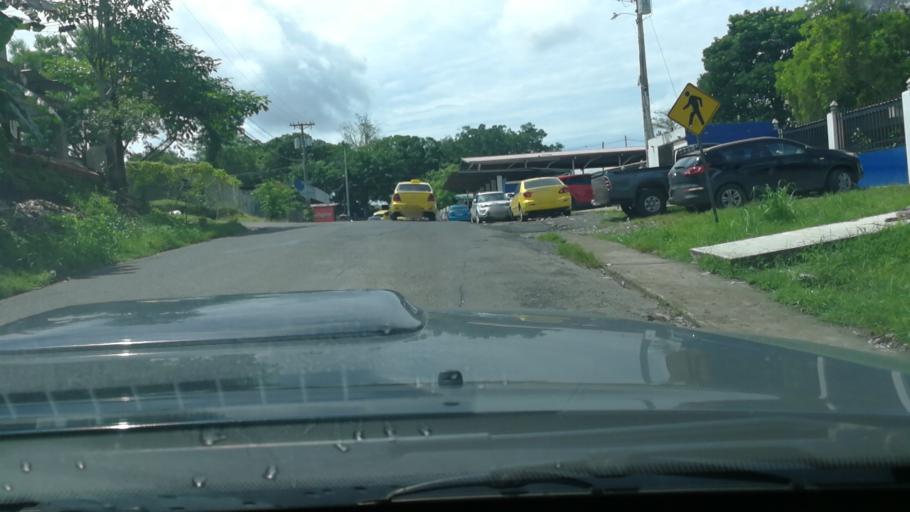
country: PA
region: Panama
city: Tocumen
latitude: 9.0947
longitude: -79.4076
